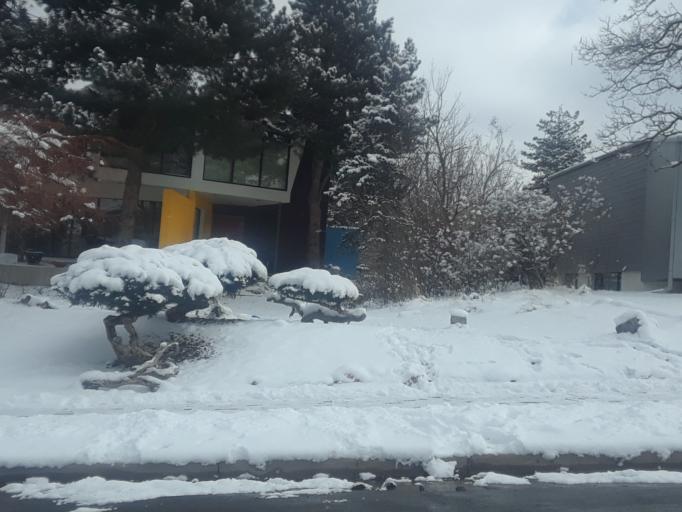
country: US
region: Colorado
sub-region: Boulder County
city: Boulder
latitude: 40.0013
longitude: -105.2867
